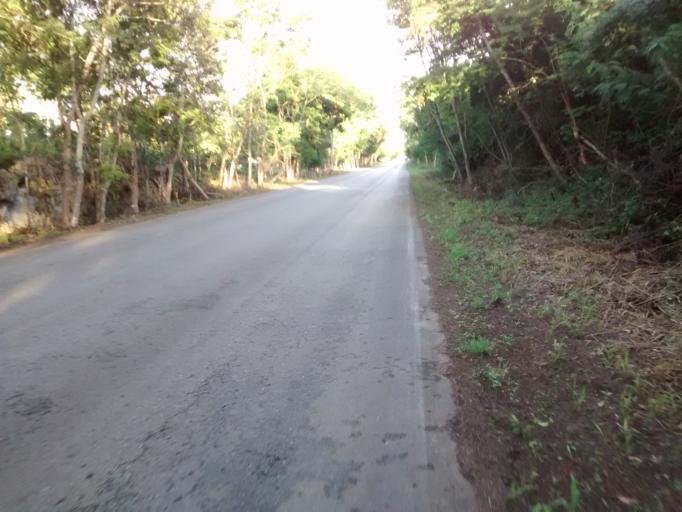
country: MX
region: Yucatan
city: Valladolid
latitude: 20.7312
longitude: -88.2212
